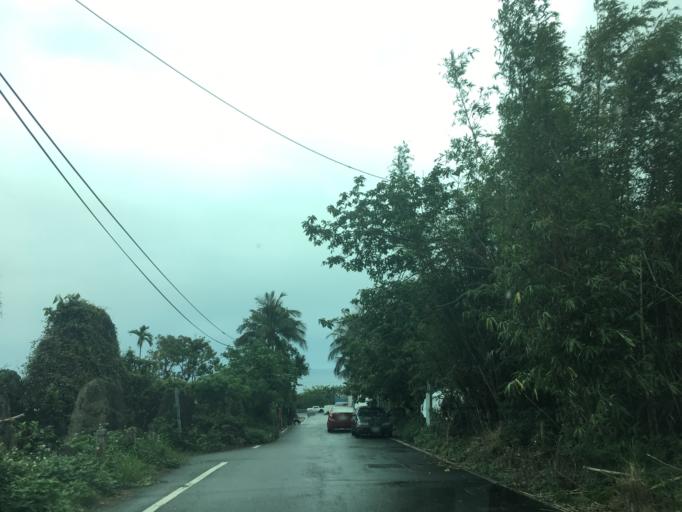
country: TW
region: Taiwan
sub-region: Taitung
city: Taitung
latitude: 22.8703
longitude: 121.2226
